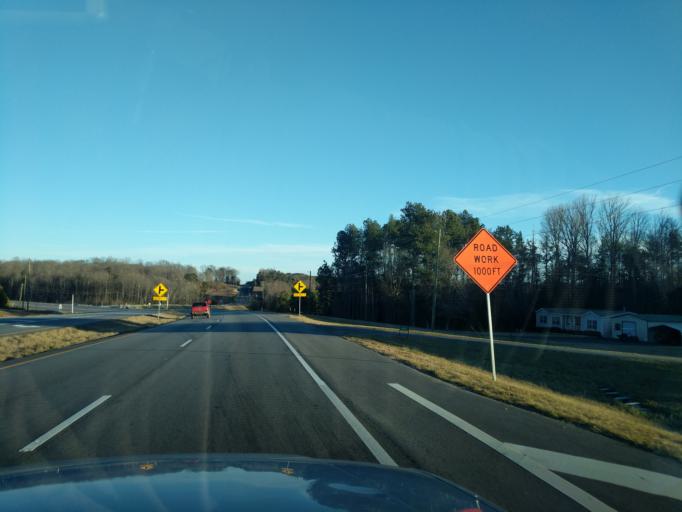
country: US
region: Georgia
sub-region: Stephens County
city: Toccoa
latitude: 34.5214
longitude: -83.2419
